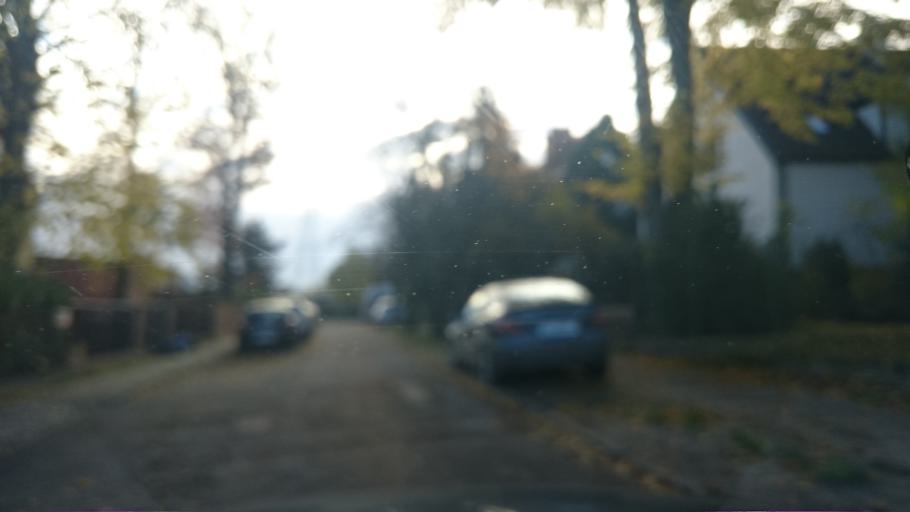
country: PL
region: Pomeranian Voivodeship
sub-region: Sopot
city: Sopot
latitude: 54.3981
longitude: 18.5811
